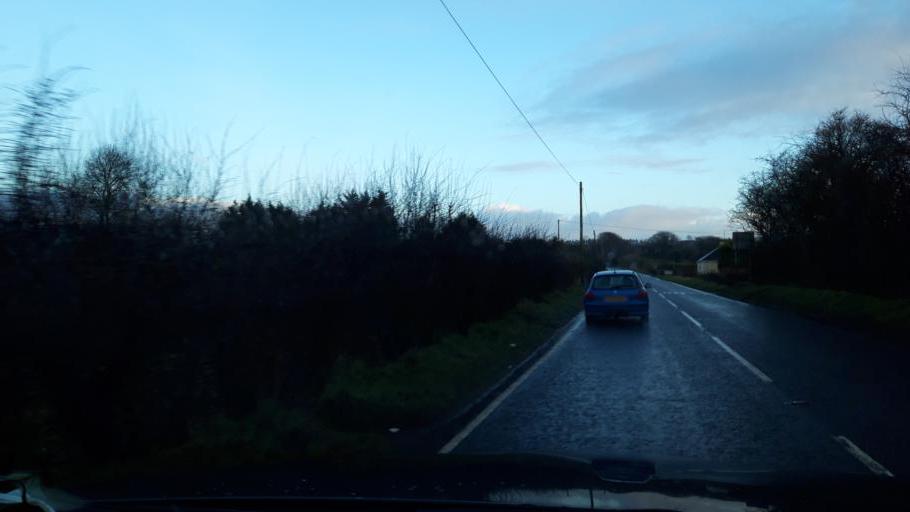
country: GB
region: Northern Ireland
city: Dunloy
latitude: 55.0326
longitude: -6.3626
